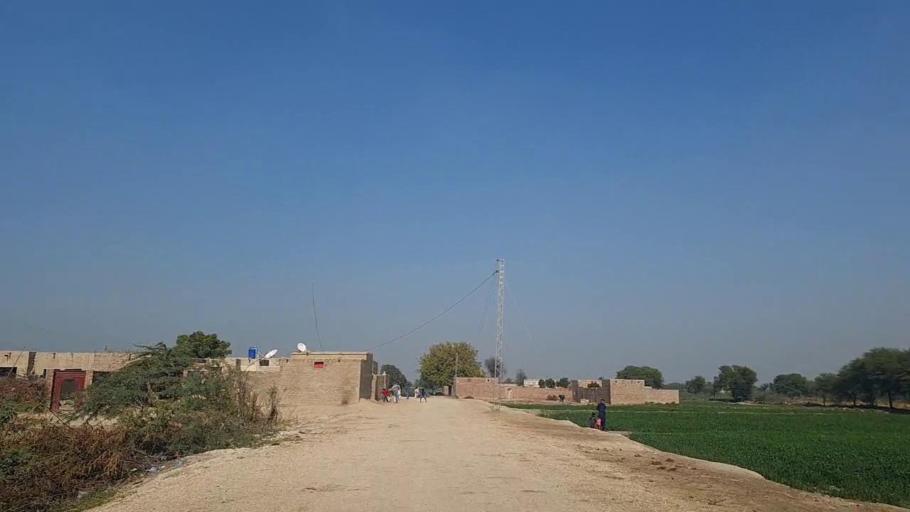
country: PK
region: Sindh
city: Nawabshah
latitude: 26.2294
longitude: 68.3425
